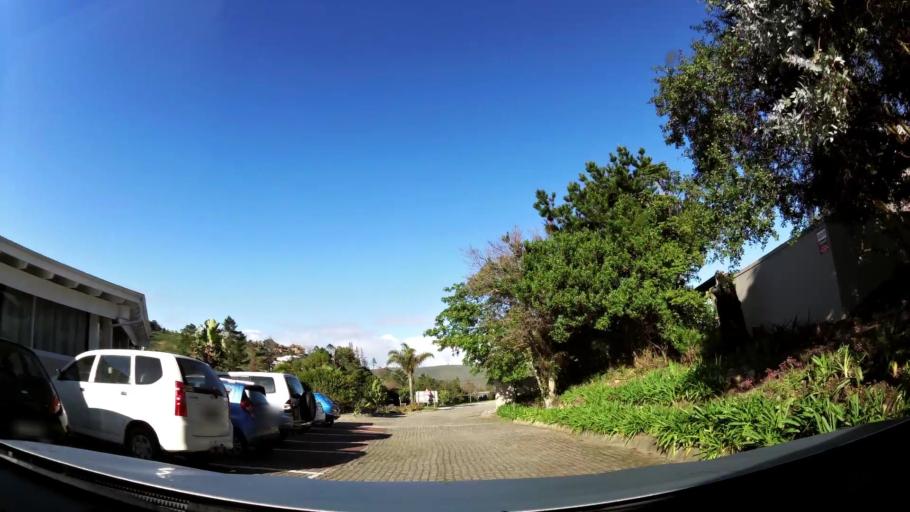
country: ZA
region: Western Cape
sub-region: Eden District Municipality
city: Knysna
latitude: -34.0328
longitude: 23.0206
